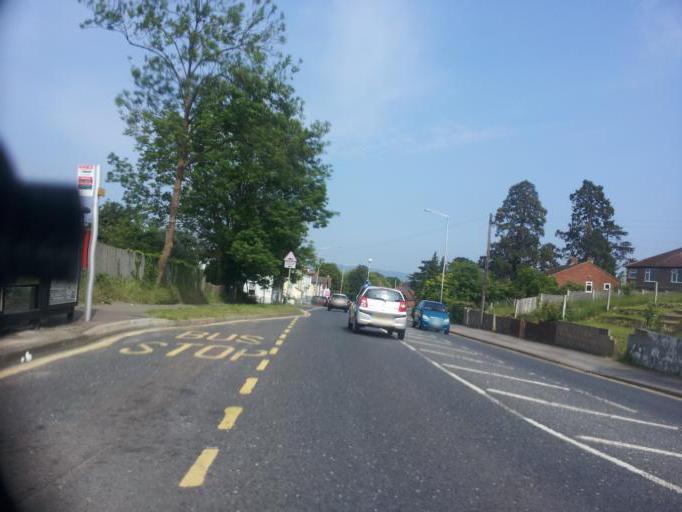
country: GB
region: England
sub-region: Kent
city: Larkfield
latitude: 51.2996
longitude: 0.4491
